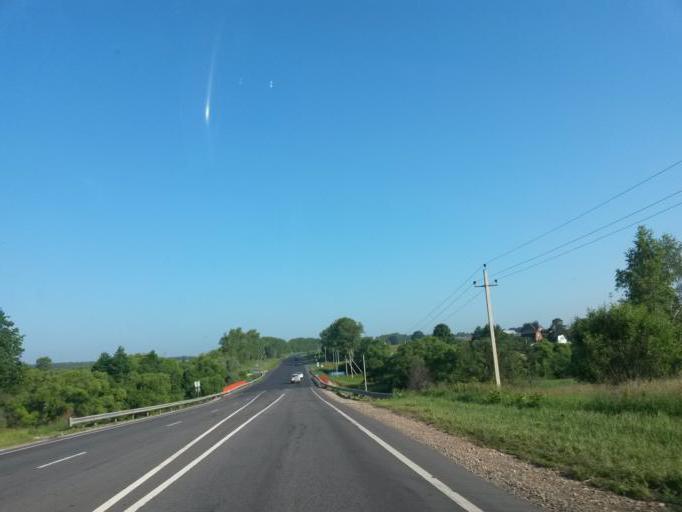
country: RU
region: Moskovskaya
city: Barybino
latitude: 55.2512
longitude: 37.8423
